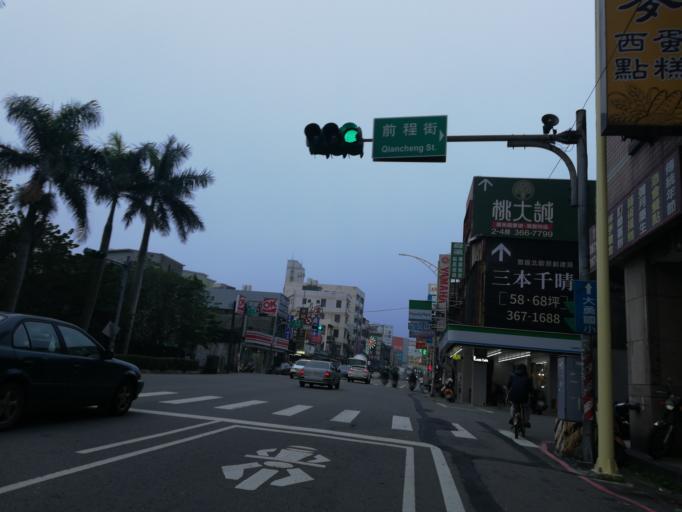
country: TW
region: Taiwan
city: Taoyuan City
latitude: 24.9710
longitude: 121.3016
